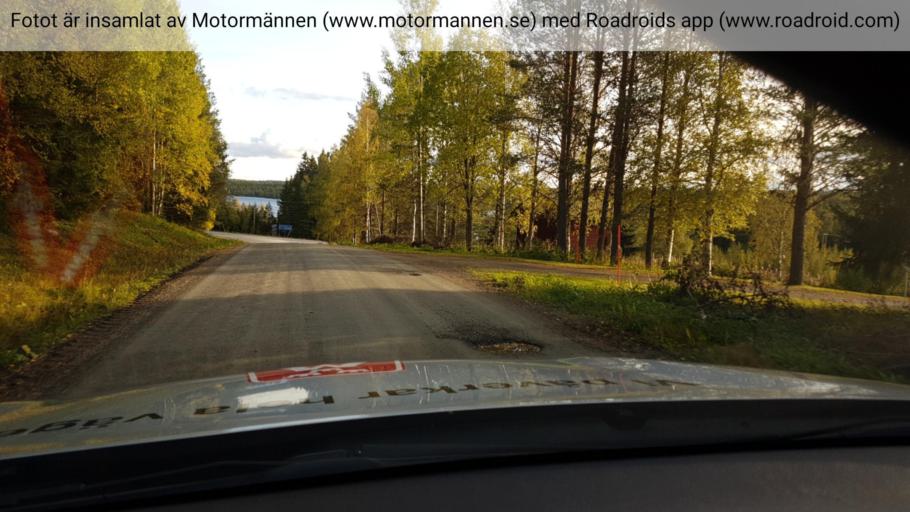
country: SE
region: Jaemtland
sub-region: Krokoms Kommun
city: Krokom
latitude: 63.6776
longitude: 14.5783
